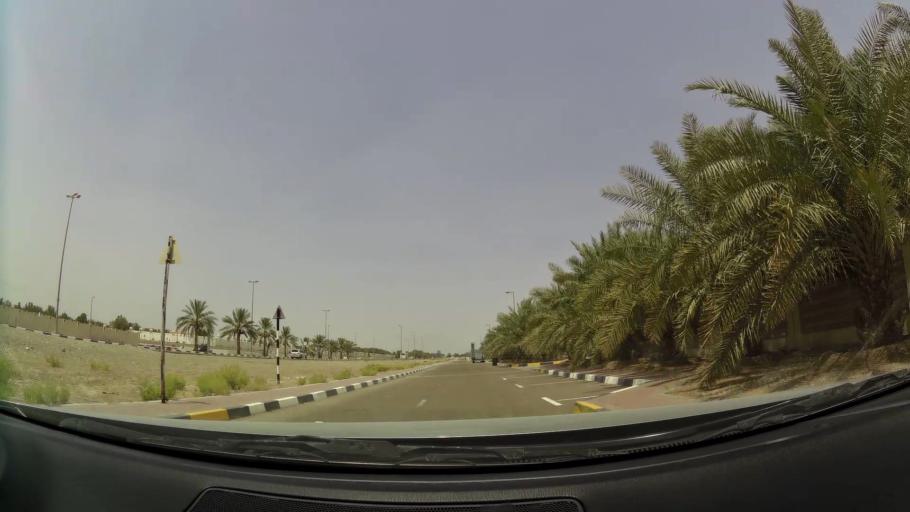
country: AE
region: Abu Dhabi
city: Al Ain
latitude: 24.1883
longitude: 55.6898
